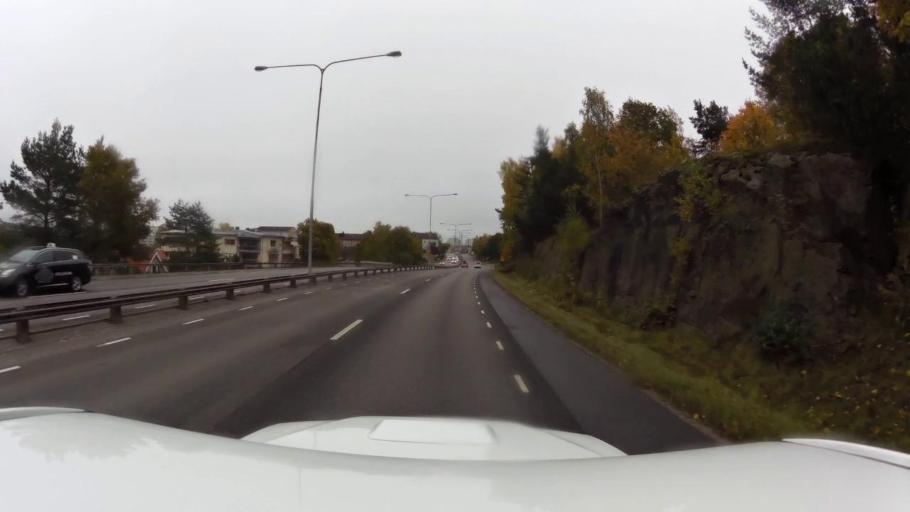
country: SE
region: OEstergoetland
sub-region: Linkopings Kommun
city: Linkoping
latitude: 58.3998
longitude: 15.6444
